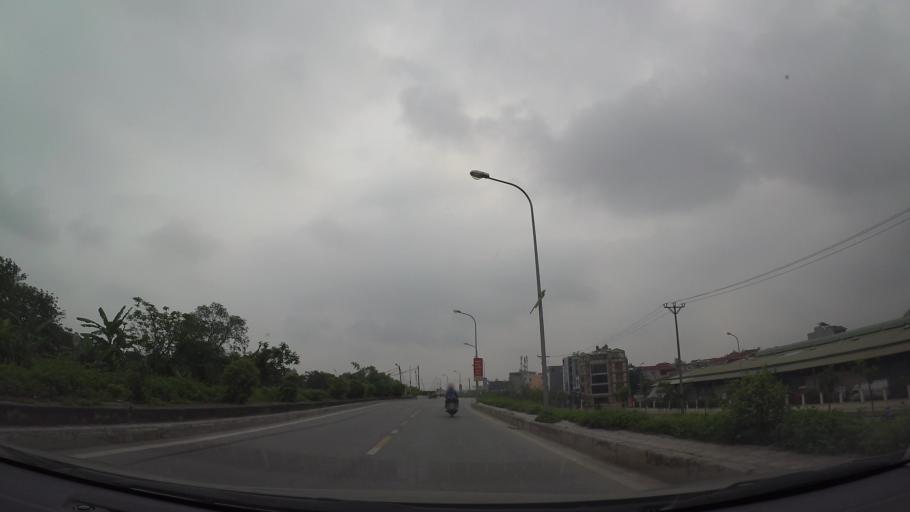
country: VN
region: Ha Noi
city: Hoan Kiem
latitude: 21.0725
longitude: 105.8862
